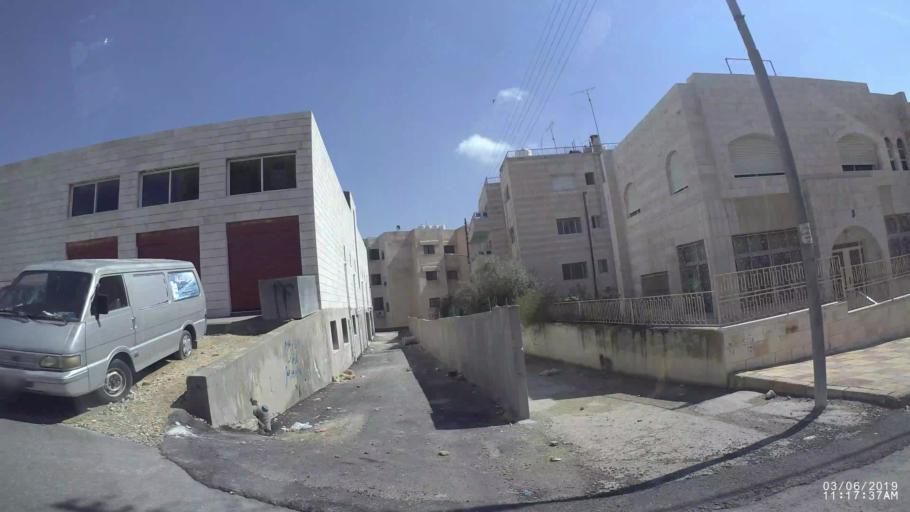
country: JO
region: Amman
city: Amman
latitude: 31.9756
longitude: 35.9910
